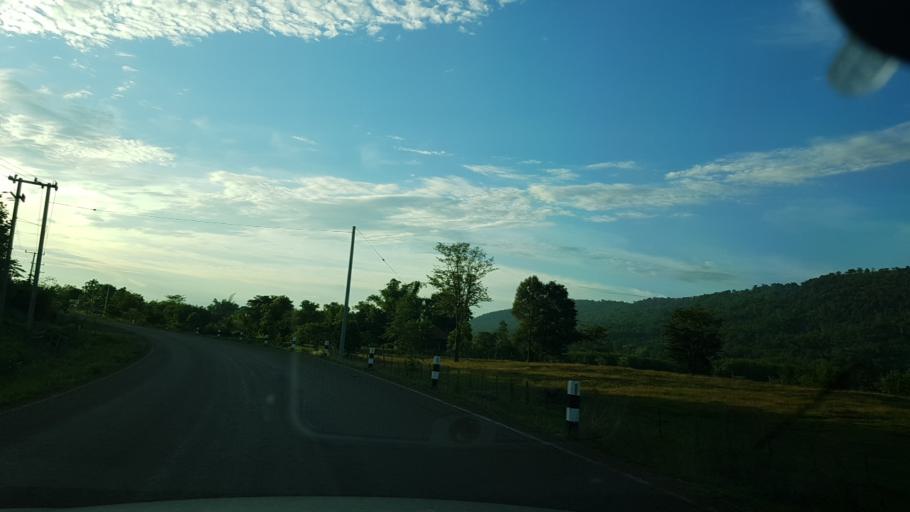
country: TH
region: Nong Khai
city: Sangkhom
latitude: 18.1475
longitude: 102.2752
